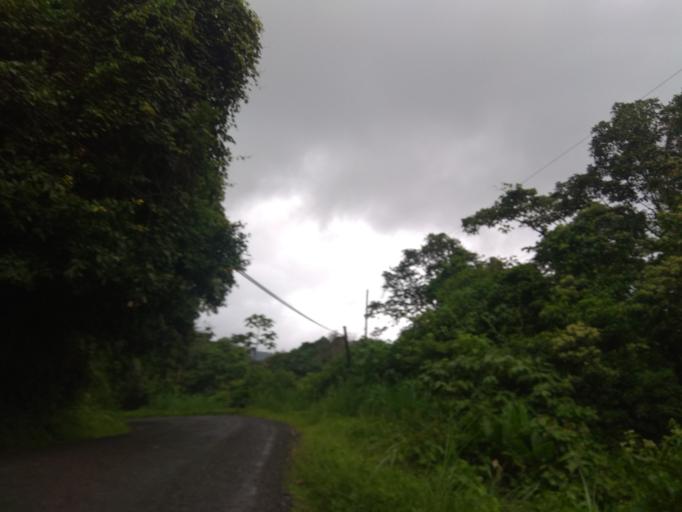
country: CR
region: Alajuela
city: La Fortuna
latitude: 10.4319
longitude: -84.7397
